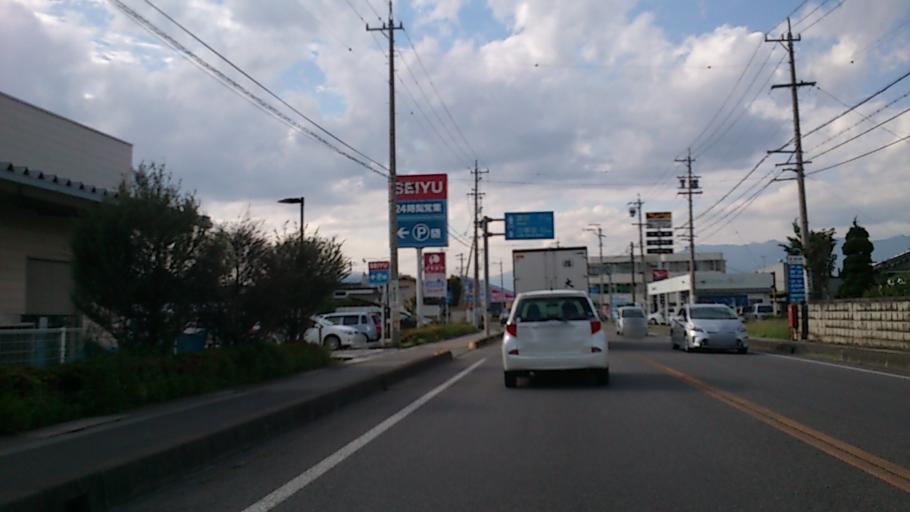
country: JP
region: Nagano
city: Saku
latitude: 36.2266
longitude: 138.4661
